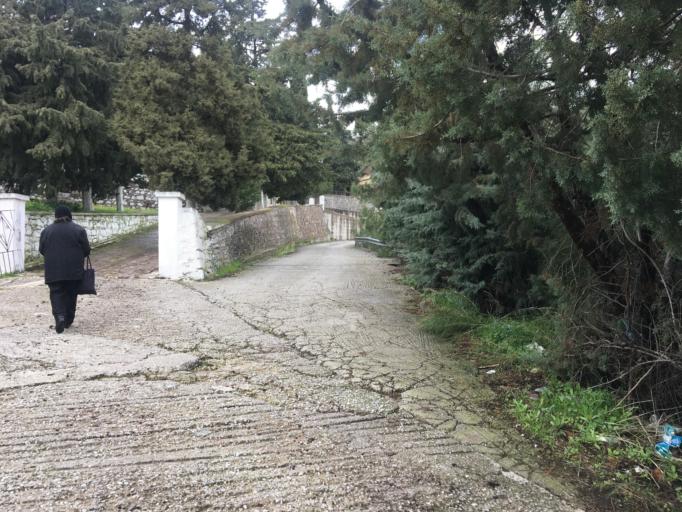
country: GR
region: North Aegean
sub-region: Nomos Lesvou
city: Agia Paraskevi
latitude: 39.2501
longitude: 26.2683
